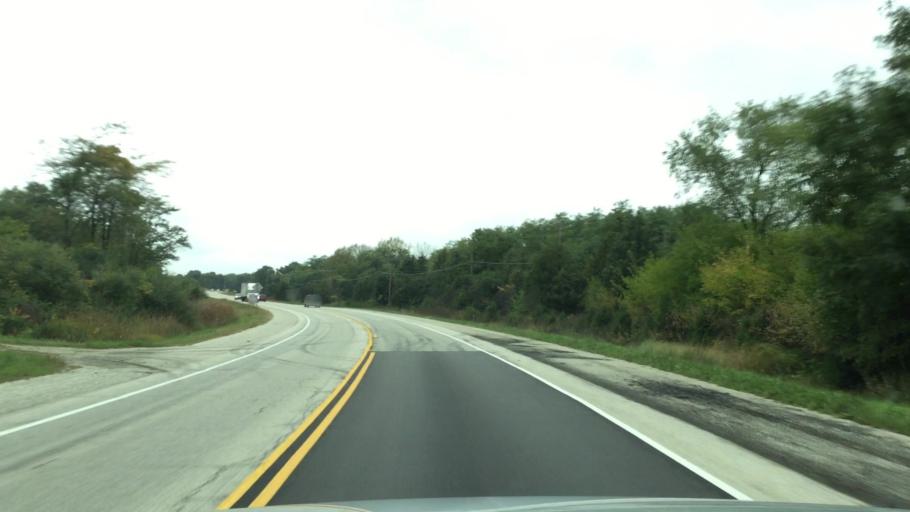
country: US
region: Wisconsin
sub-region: Racine County
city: Eagle Lake
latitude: 42.7422
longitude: -88.0863
